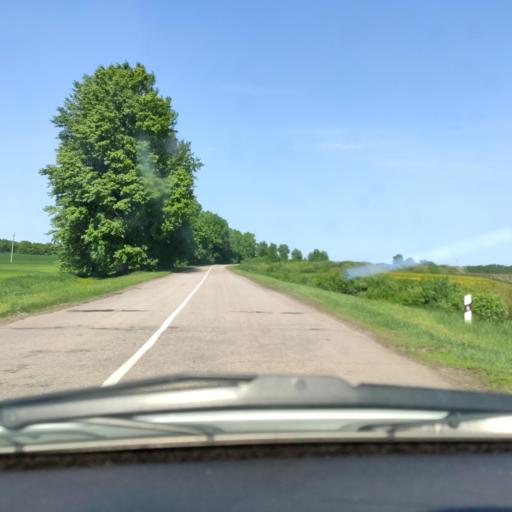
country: RU
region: Bashkortostan
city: Chishmy
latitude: 54.4814
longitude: 55.5709
